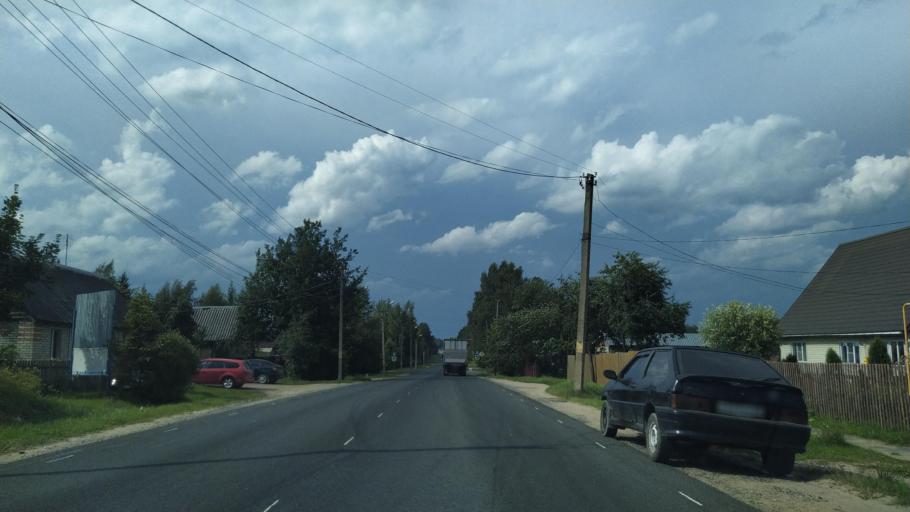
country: RU
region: Pskov
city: Porkhov
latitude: 57.7808
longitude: 29.5398
